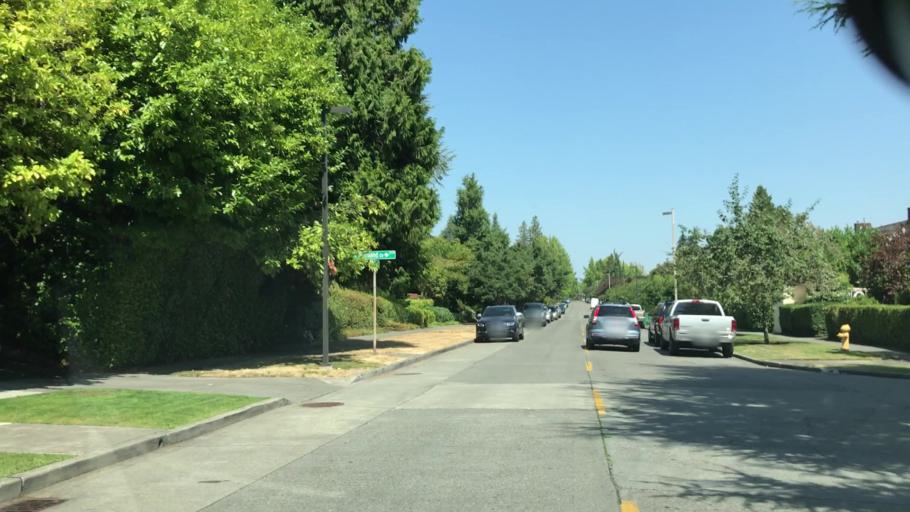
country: US
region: Washington
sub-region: King County
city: Medina
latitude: 47.6296
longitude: -122.2814
